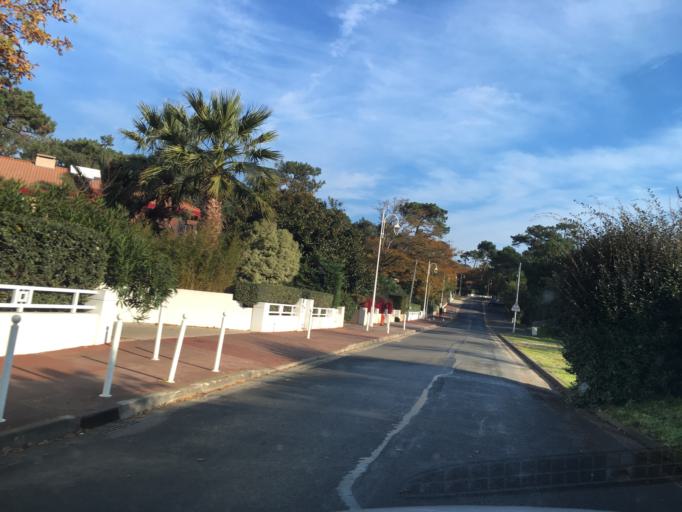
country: FR
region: Aquitaine
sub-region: Departement de la Gironde
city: Arcachon
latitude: 44.6524
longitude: -1.1943
